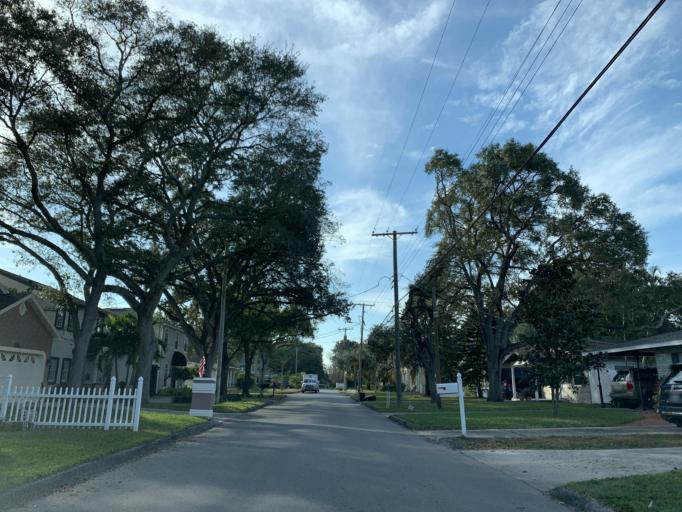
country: US
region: Florida
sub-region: Hillsborough County
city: Tampa
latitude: 27.8967
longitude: -82.4987
